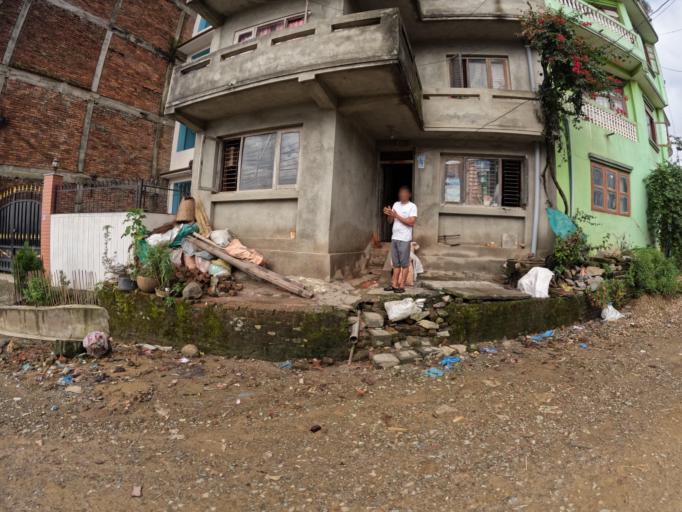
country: NP
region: Central Region
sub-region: Bagmati Zone
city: Kathmandu
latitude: 27.7678
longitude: 85.3316
